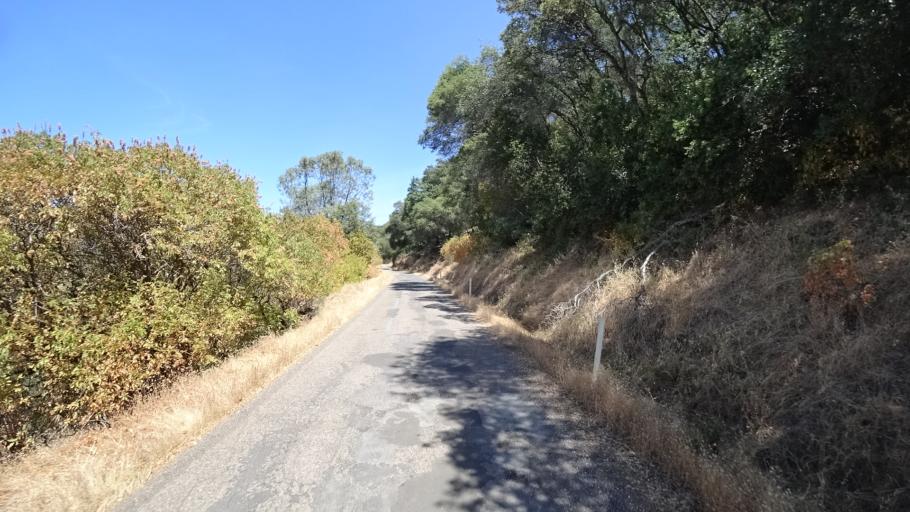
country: US
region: California
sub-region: Amador County
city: Jackson
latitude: 38.2886
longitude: -120.7212
